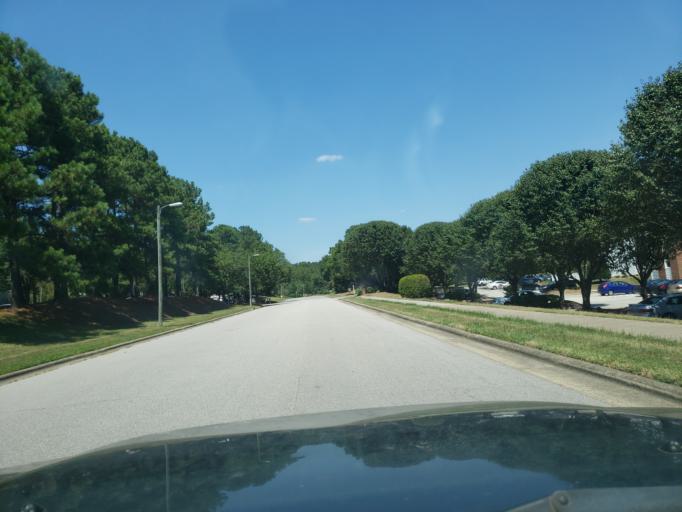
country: US
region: North Carolina
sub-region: Durham County
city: Durham
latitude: 35.9092
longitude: -78.9478
